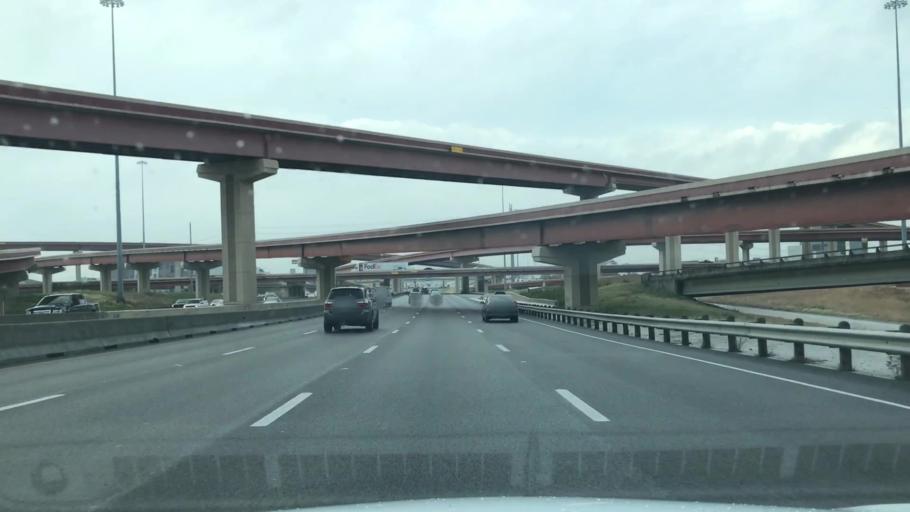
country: US
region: Texas
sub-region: Tarrant County
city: Euless
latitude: 32.8372
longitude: -97.0137
